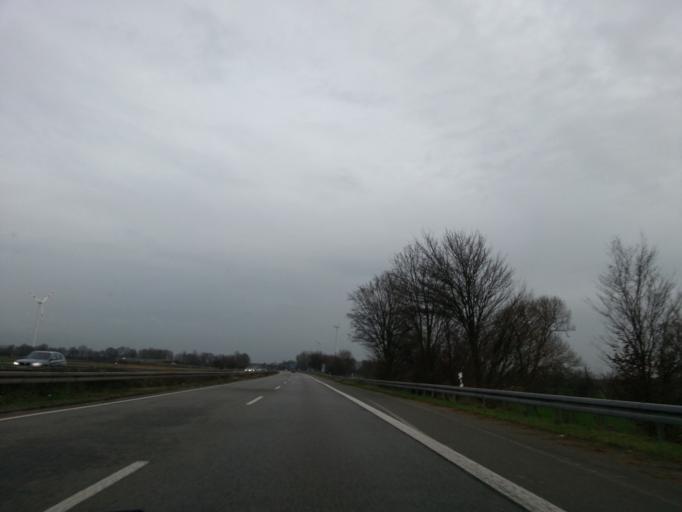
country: DE
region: North Rhine-Westphalia
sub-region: Regierungsbezirk Dusseldorf
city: Emmerich
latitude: 51.8638
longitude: 6.2329
